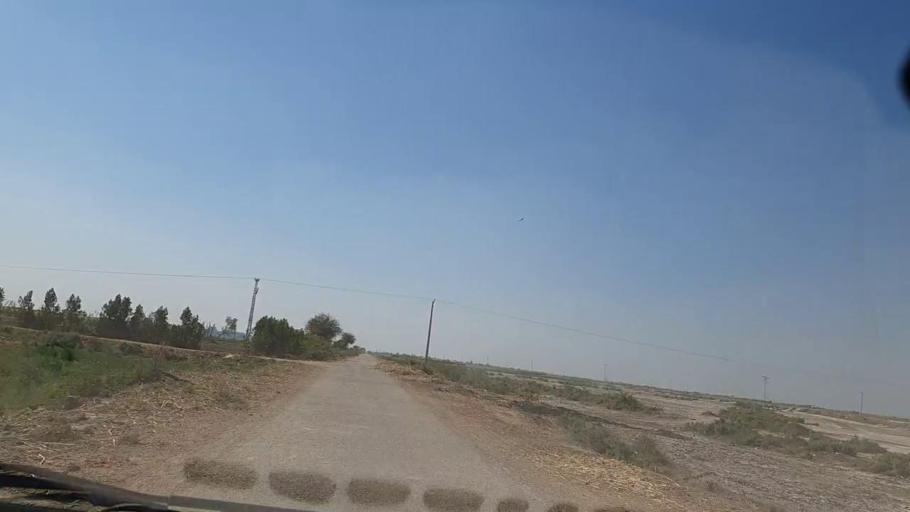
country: PK
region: Sindh
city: Mirwah Gorchani
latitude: 25.3744
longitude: 69.0172
